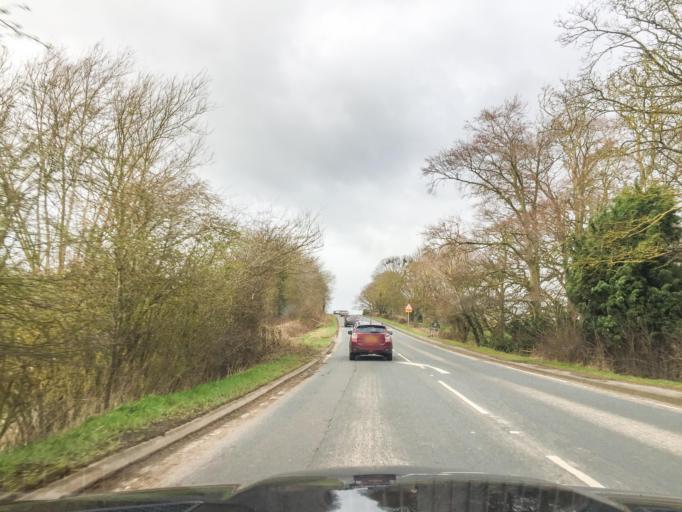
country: GB
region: England
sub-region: Warwickshire
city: Shipston on Stour
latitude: 52.0730
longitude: -1.6198
